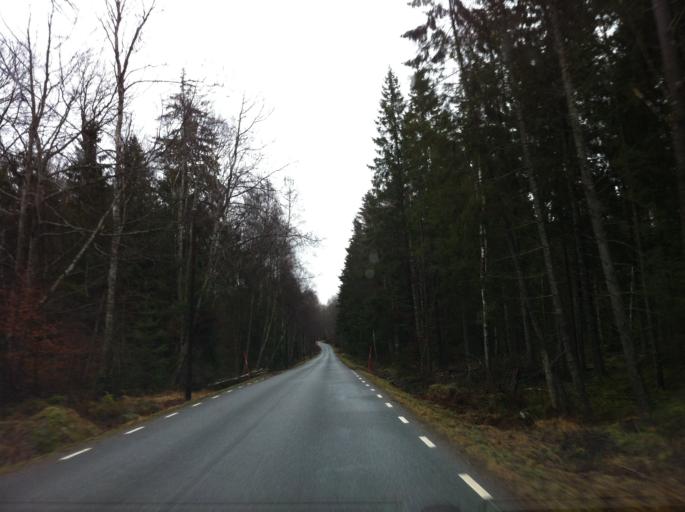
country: SE
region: Blekinge
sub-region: Olofstroms Kommun
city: Olofstroem
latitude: 56.3635
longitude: 14.5082
